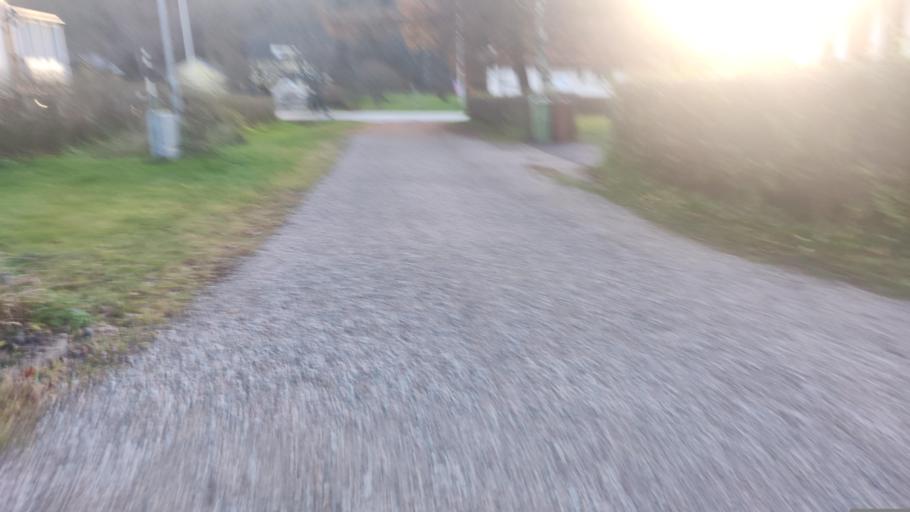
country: SE
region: Vaesternorrland
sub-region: Sundsvalls Kommun
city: Kvissleby
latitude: 62.3112
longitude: 17.3661
